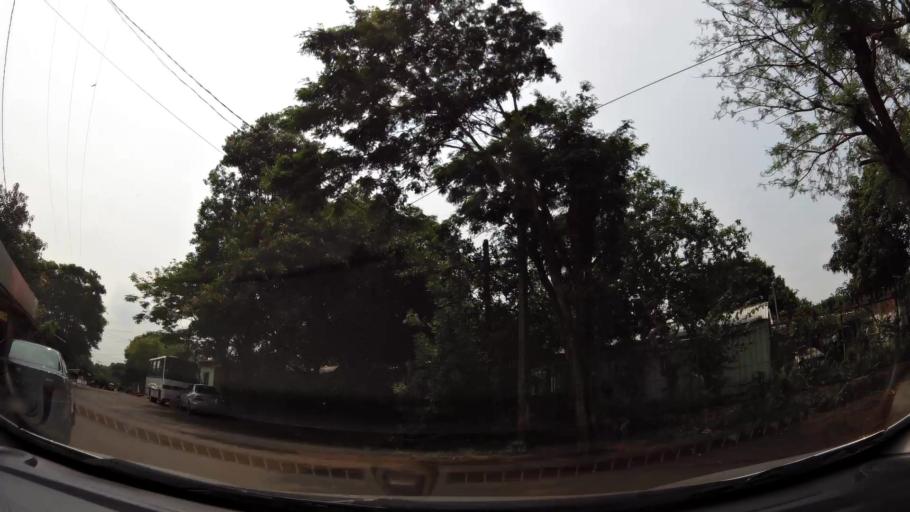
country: PY
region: Alto Parana
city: Presidente Franco
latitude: -25.5672
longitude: -54.6167
